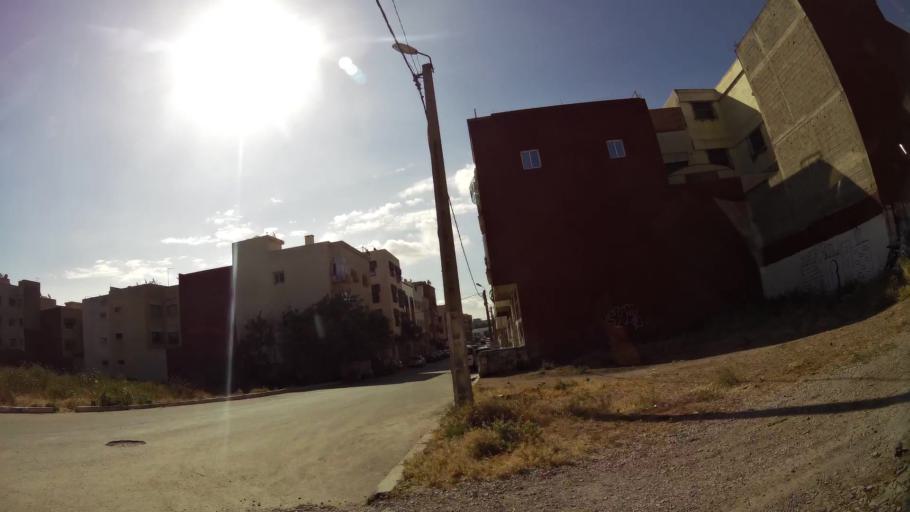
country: MA
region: Rabat-Sale-Zemmour-Zaer
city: Sale
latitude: 34.0573
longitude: -6.8119
